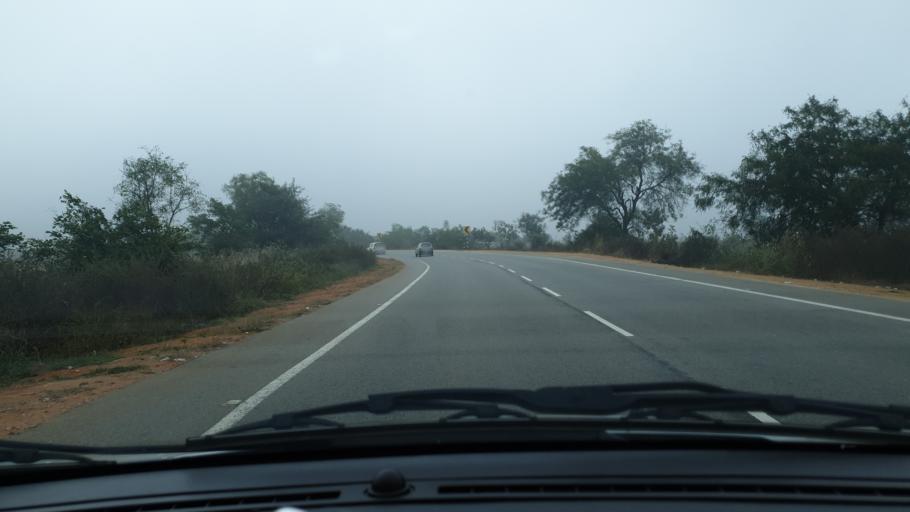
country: IN
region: Telangana
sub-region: Nalgonda
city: Devarkonda
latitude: 16.6307
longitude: 78.6438
